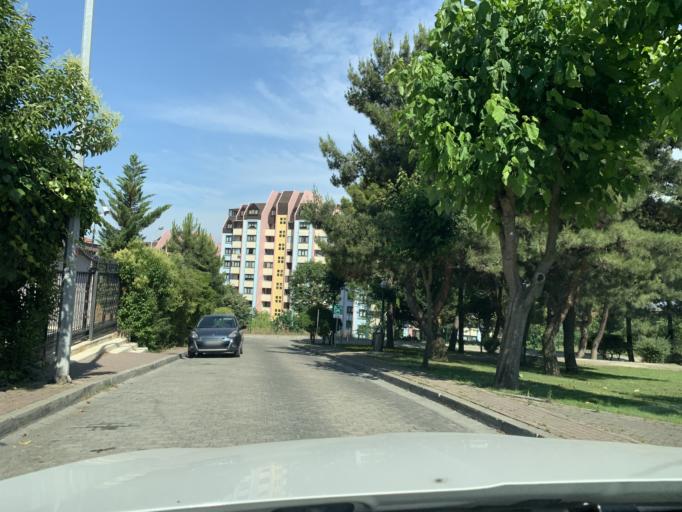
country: TR
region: Istanbul
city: Esenyurt
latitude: 41.0639
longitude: 28.6799
